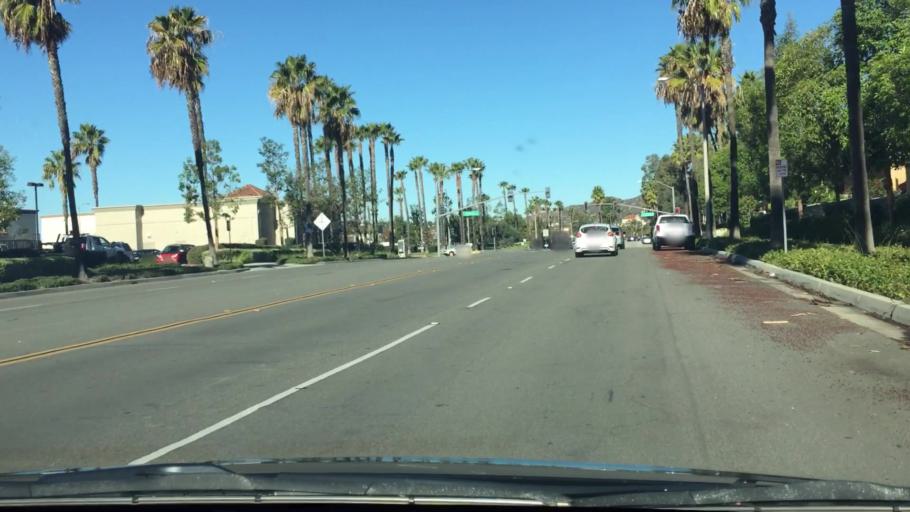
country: US
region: California
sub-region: Orange County
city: Rancho Santa Margarita
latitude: 33.6363
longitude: -117.5982
